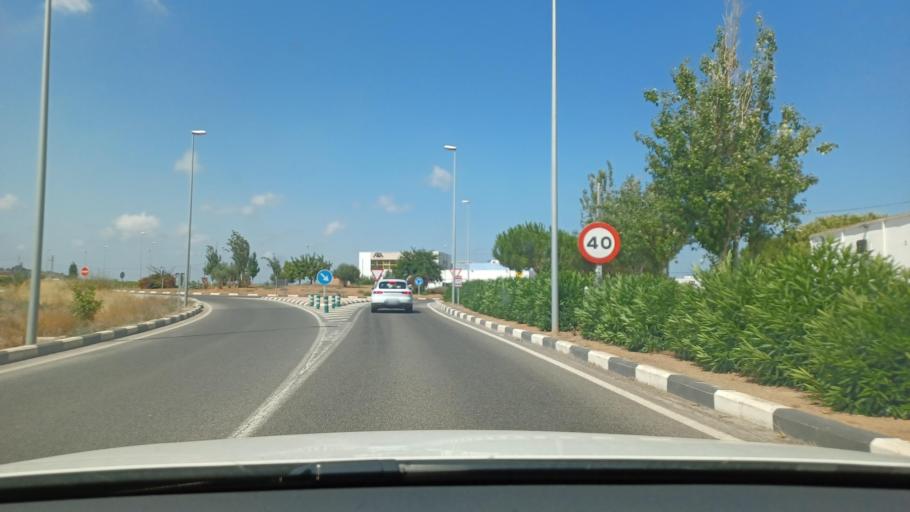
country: ES
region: Valencia
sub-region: Provincia de Castello
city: Chilches
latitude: 39.7811
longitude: -0.1935
